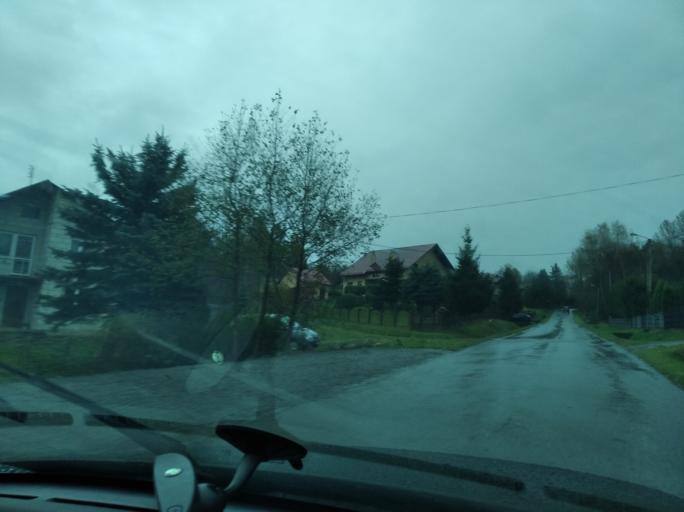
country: PL
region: Subcarpathian Voivodeship
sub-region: Powiat rzeszowski
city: Chmielnik
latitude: 49.9790
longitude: 22.1857
